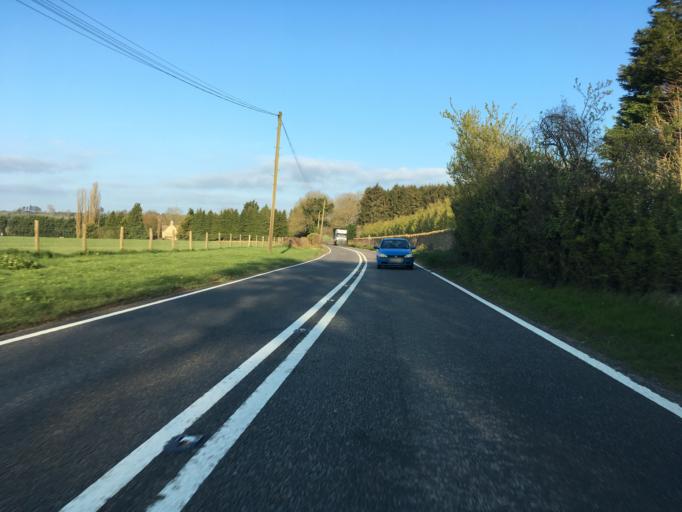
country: GB
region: England
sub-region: Gloucestershire
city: Shipton Village
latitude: 51.8670
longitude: -1.9766
